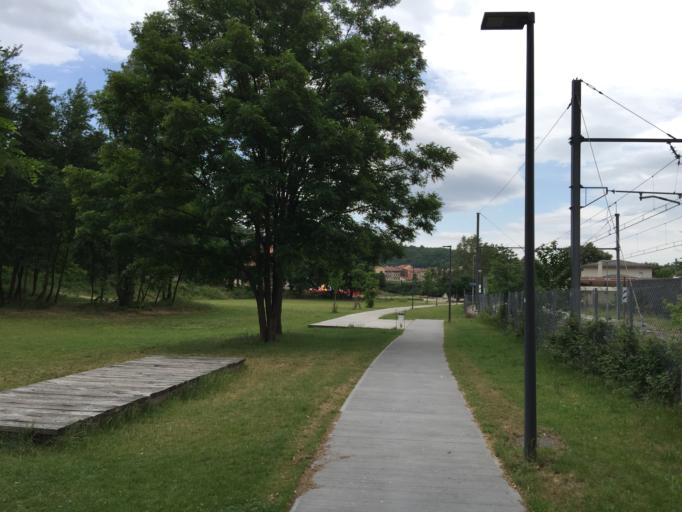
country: FR
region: Rhone-Alpes
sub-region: Departement de la Loire
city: Saint-Etienne
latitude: 45.4359
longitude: 4.3784
